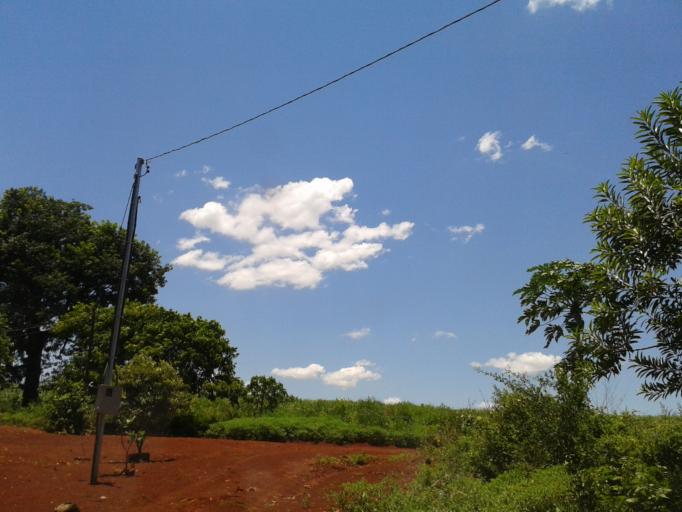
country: BR
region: Minas Gerais
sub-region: Centralina
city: Centralina
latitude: -18.6719
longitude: -49.2411
